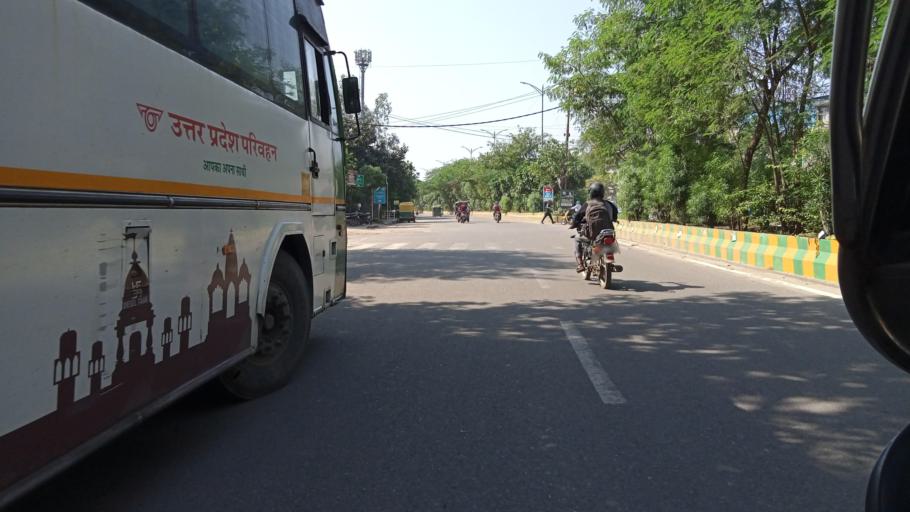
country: IN
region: Uttar Pradesh
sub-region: Ghaziabad
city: Ghaziabad
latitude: 28.6708
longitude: 77.3674
